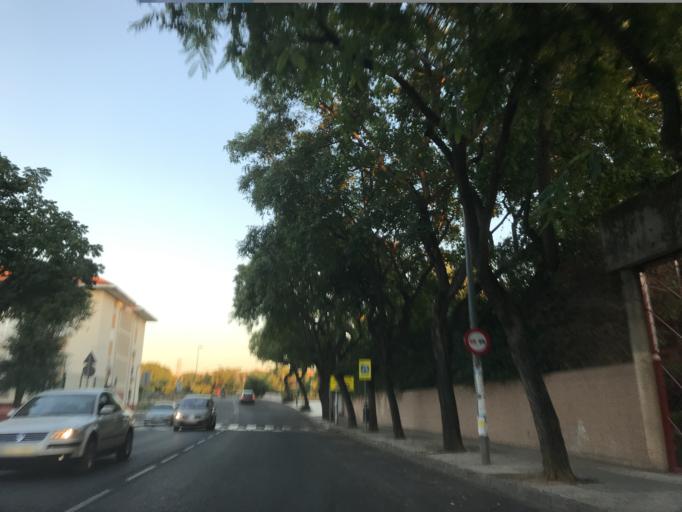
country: ES
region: Andalusia
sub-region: Provincia de Sevilla
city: Sevilla
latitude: 37.4059
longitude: -5.9261
